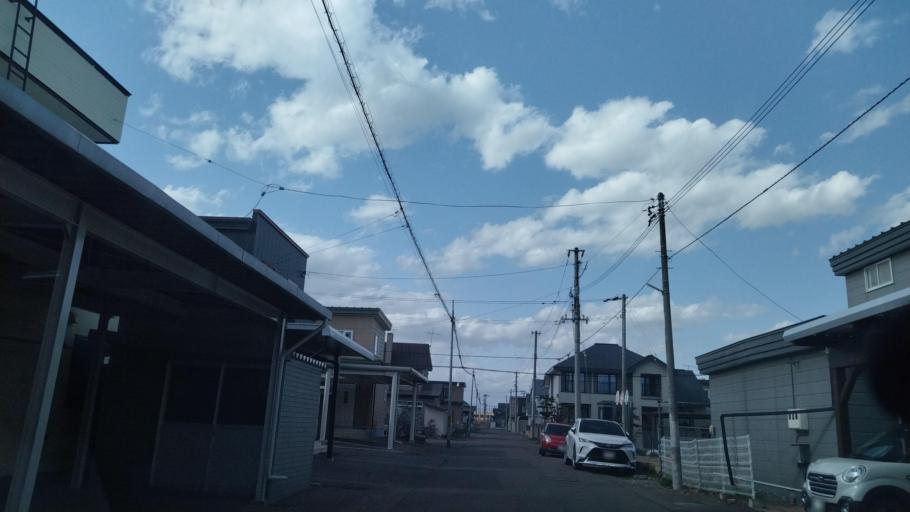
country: JP
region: Hokkaido
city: Obihiro
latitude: 42.9349
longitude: 143.1654
